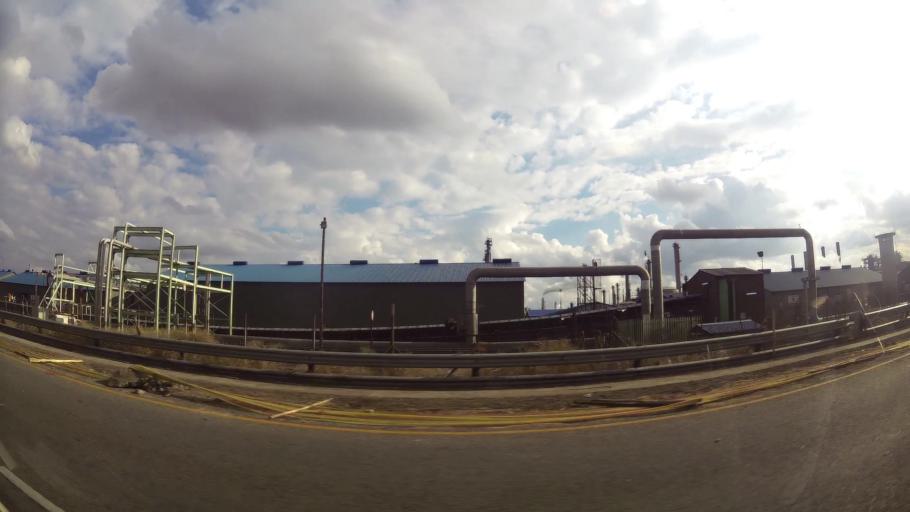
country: ZA
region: Orange Free State
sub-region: Fezile Dabi District Municipality
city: Sasolburg
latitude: -26.8238
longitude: 27.8466
